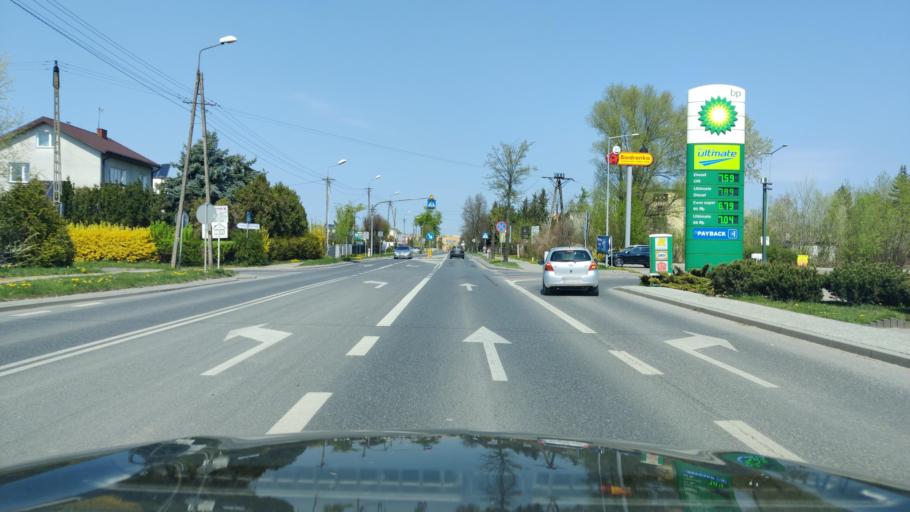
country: PL
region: Masovian Voivodeship
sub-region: Powiat pultuski
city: Pultusk
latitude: 52.6925
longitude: 21.0808
